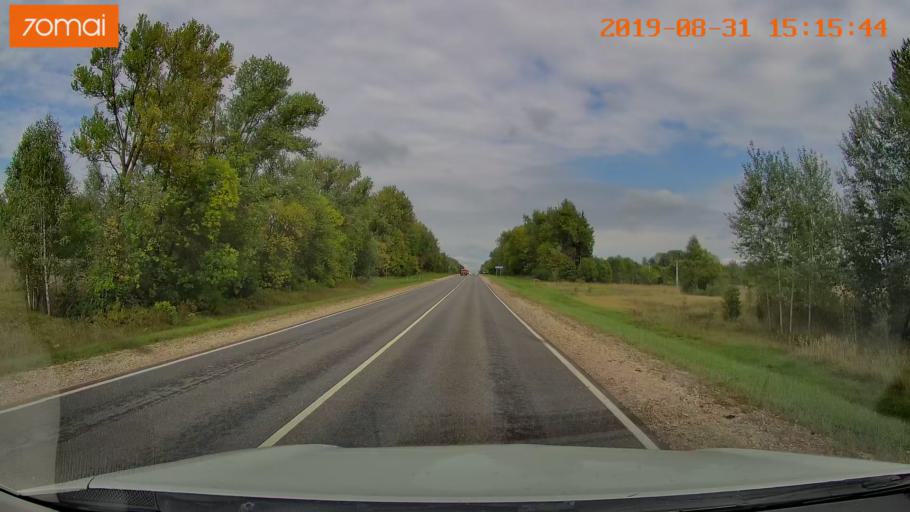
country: RU
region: Kaluga
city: Baryatino
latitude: 54.4539
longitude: 34.3333
